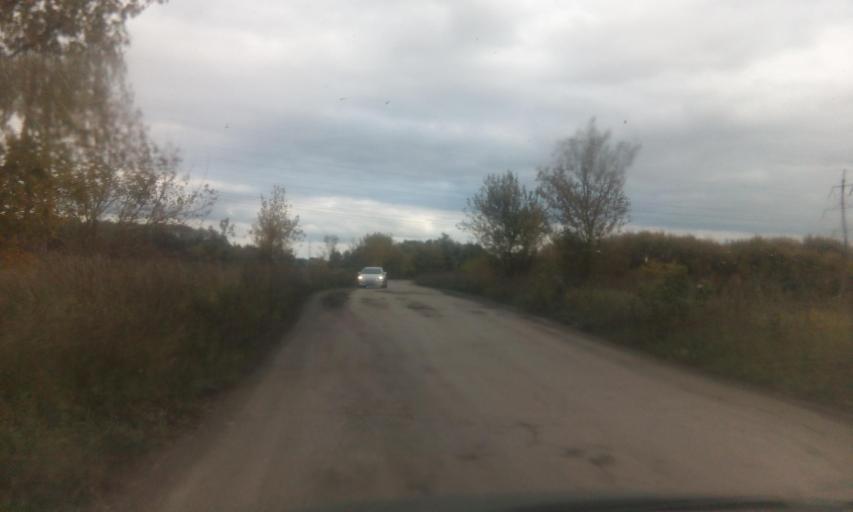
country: RU
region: Tula
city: Gritsovskiy
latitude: 54.1281
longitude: 38.1625
